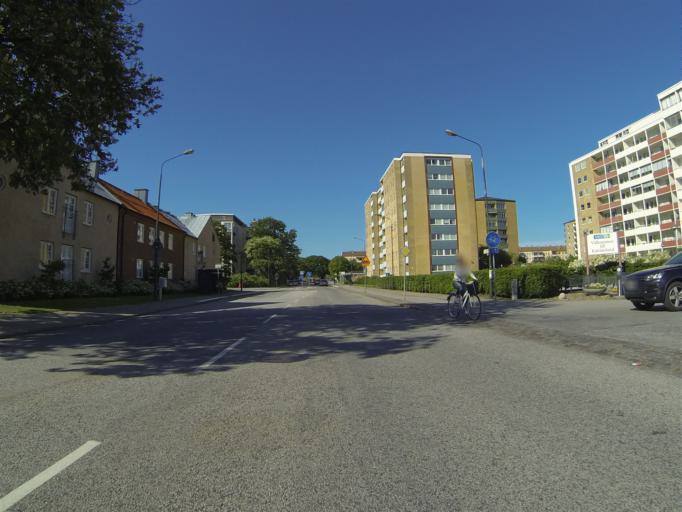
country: SE
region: Skane
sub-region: Malmo
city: Malmoe
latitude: 55.6007
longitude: 13.0316
